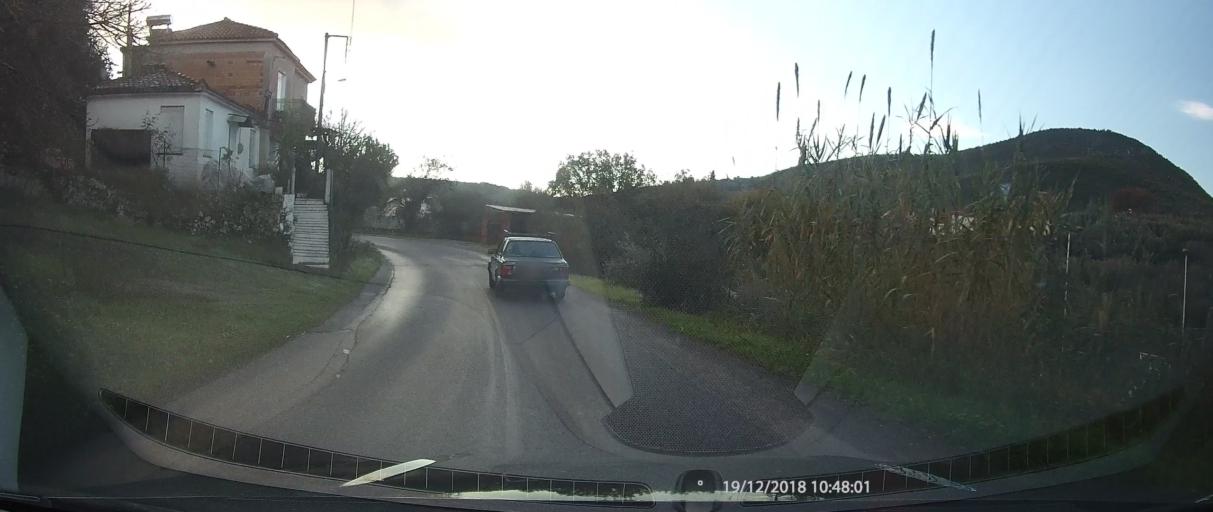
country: GR
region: Peloponnese
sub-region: Nomos Messinias
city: Kardamyli
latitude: 36.9336
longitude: 22.1884
